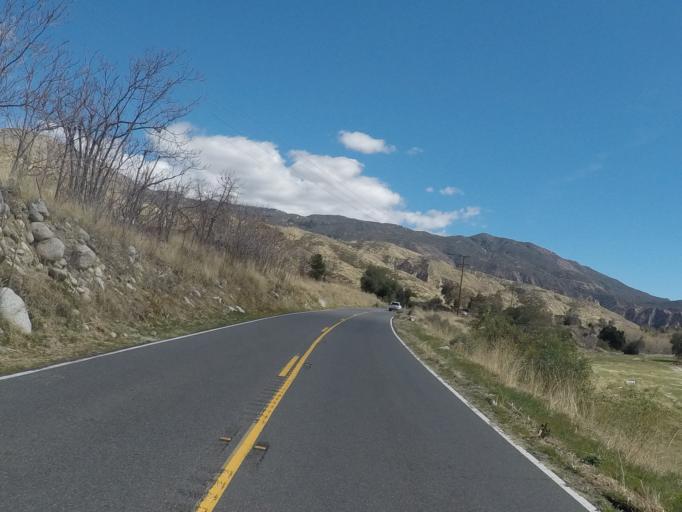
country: US
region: California
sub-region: Riverside County
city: Valle Vista
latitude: 33.7370
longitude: -116.8238
